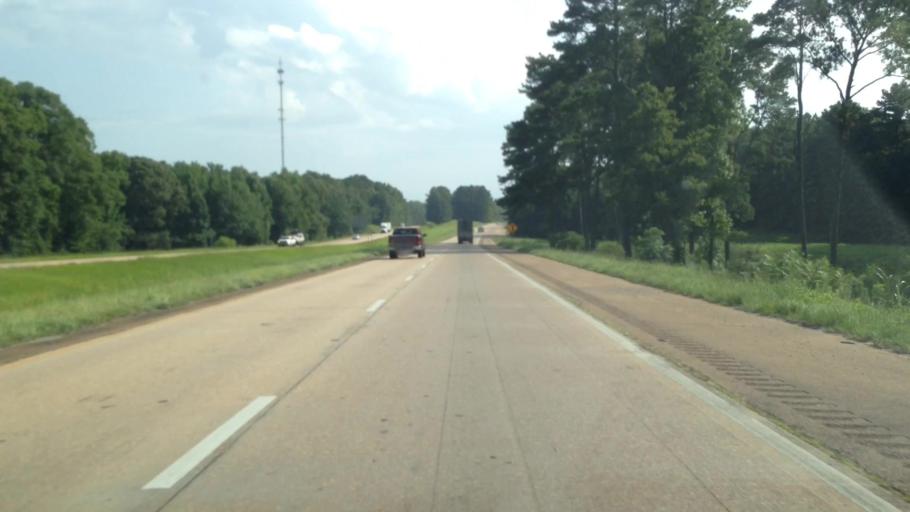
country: US
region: Mississippi
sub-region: Copiah County
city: Crystal Springs
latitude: 32.0155
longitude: -90.3614
